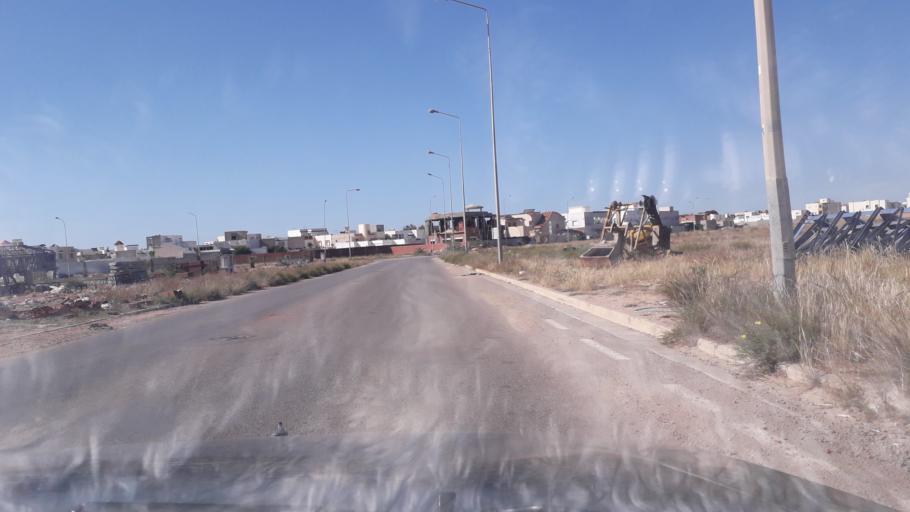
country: TN
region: Safaqis
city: Al Qarmadah
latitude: 34.8293
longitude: 10.7535
